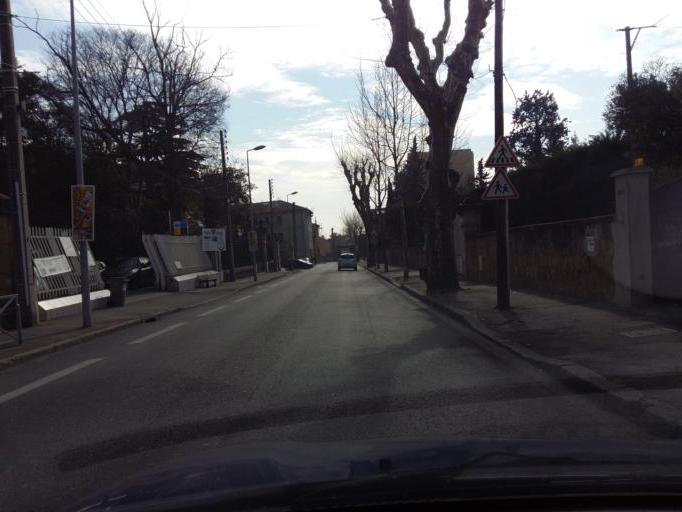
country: FR
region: Provence-Alpes-Cote d'Azur
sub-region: Departement des Bouches-du-Rhone
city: Salon-de-Provence
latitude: 43.6459
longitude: 5.0937
